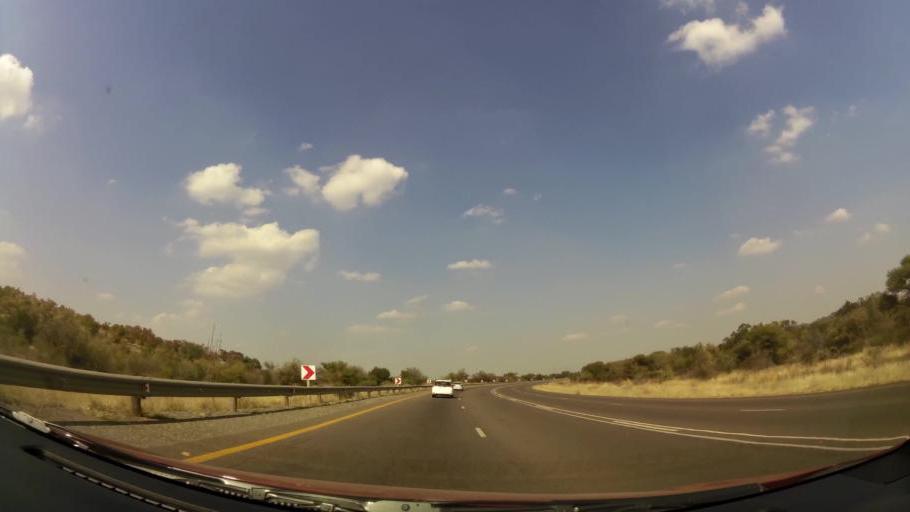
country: ZA
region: North-West
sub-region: Bojanala Platinum District Municipality
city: Mogwase
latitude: -25.4376
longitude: 27.0872
